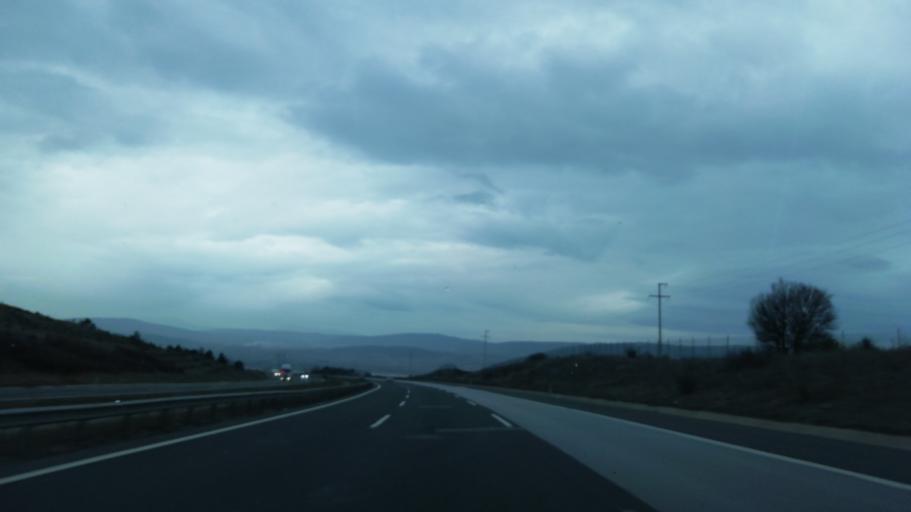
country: TR
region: Bolu
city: Yenicaga
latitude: 40.7624
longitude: 32.0599
